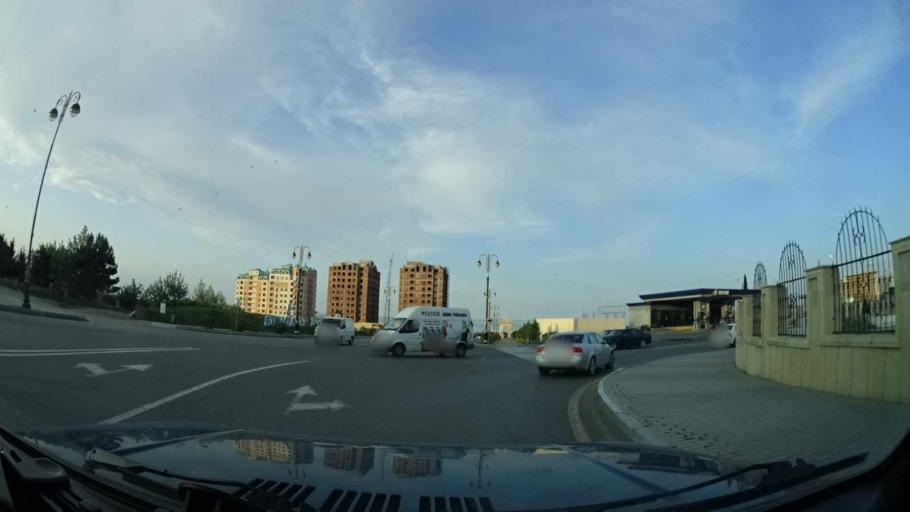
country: AZ
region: Sumqayit
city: Corat
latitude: 40.5822
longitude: 49.6883
